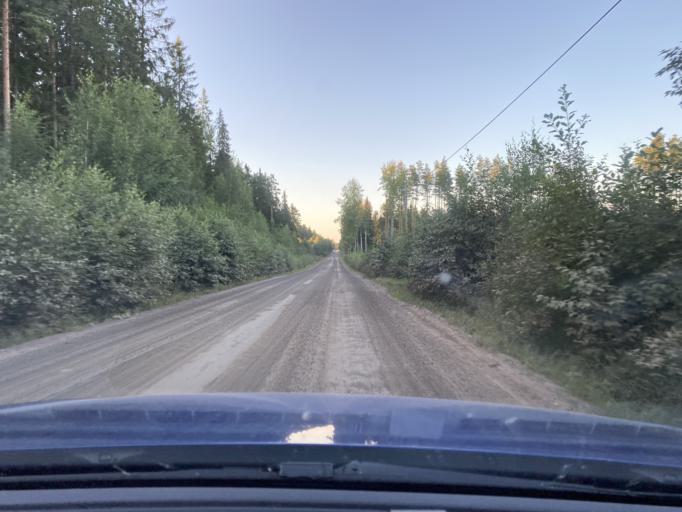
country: FI
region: Satakunta
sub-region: Rauma
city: Kiukainen
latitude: 61.1378
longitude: 21.9919
